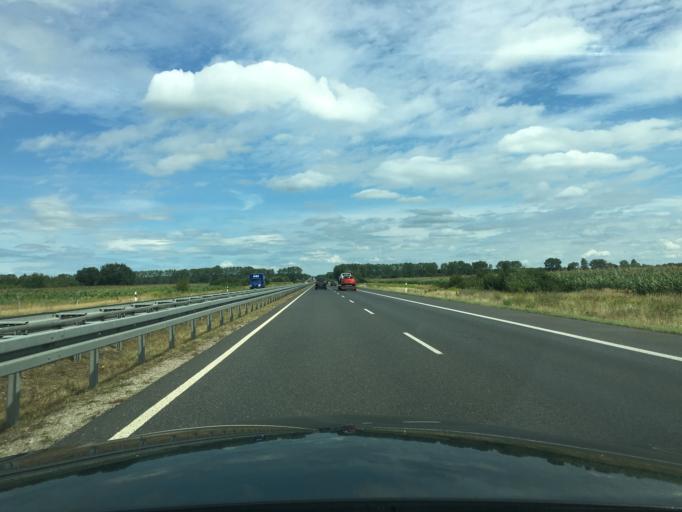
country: DE
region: Brandenburg
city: Oranienburg
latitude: 52.7680
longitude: 13.2112
